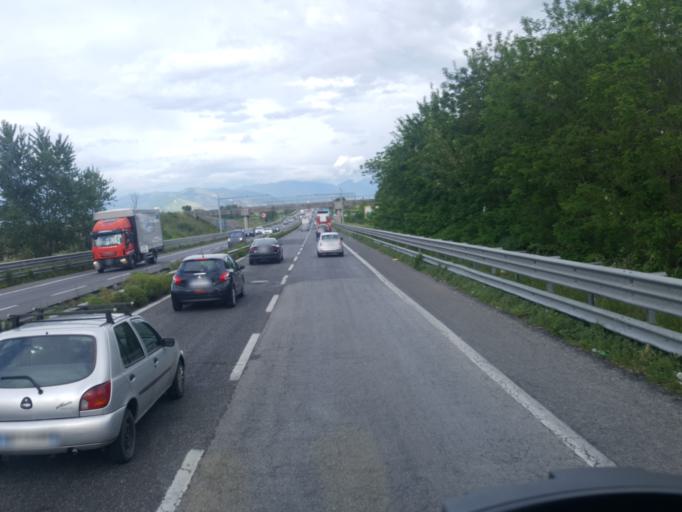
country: IT
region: Campania
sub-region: Provincia di Napoli
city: Pascarola
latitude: 40.9734
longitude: 14.3155
